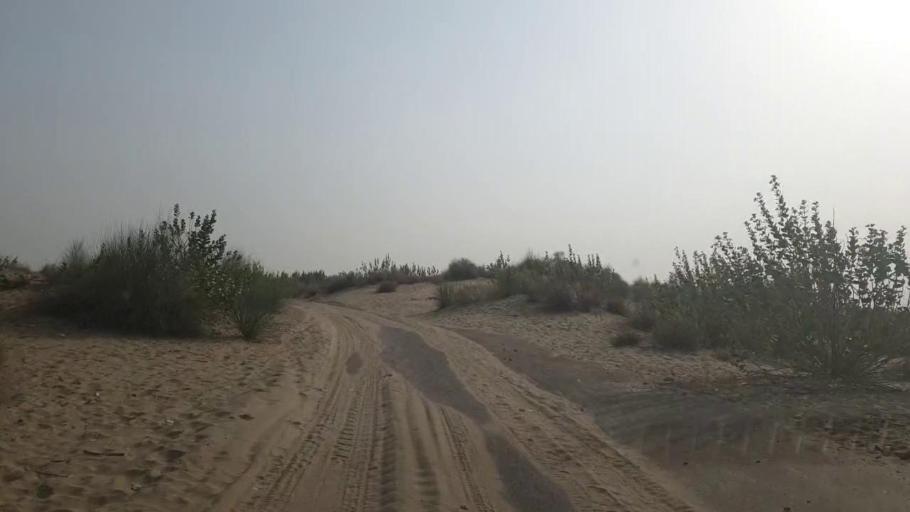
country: PK
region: Sindh
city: Chor
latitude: 25.4518
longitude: 69.9625
